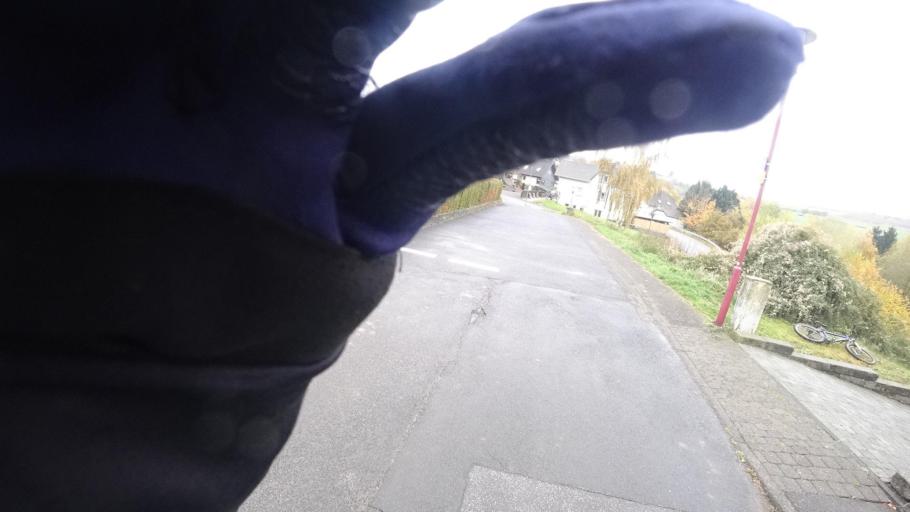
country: DE
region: Rheinland-Pfalz
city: Urbar
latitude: 50.1333
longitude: 7.7176
